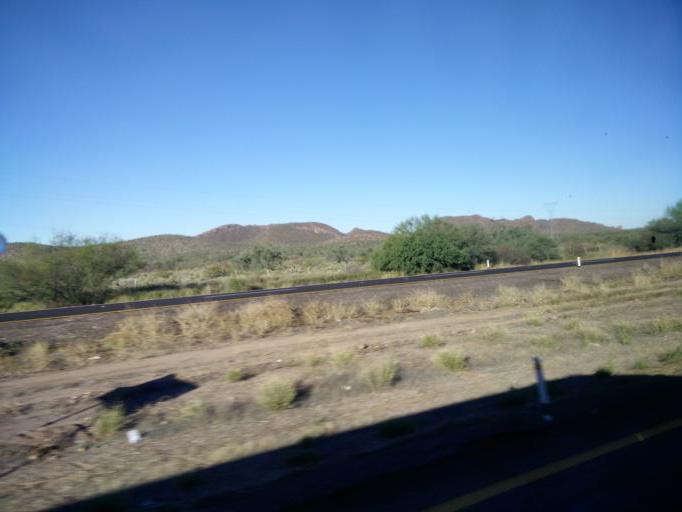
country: MX
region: Sonora
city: Heroica Guaymas
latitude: 28.2650
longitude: -111.0329
